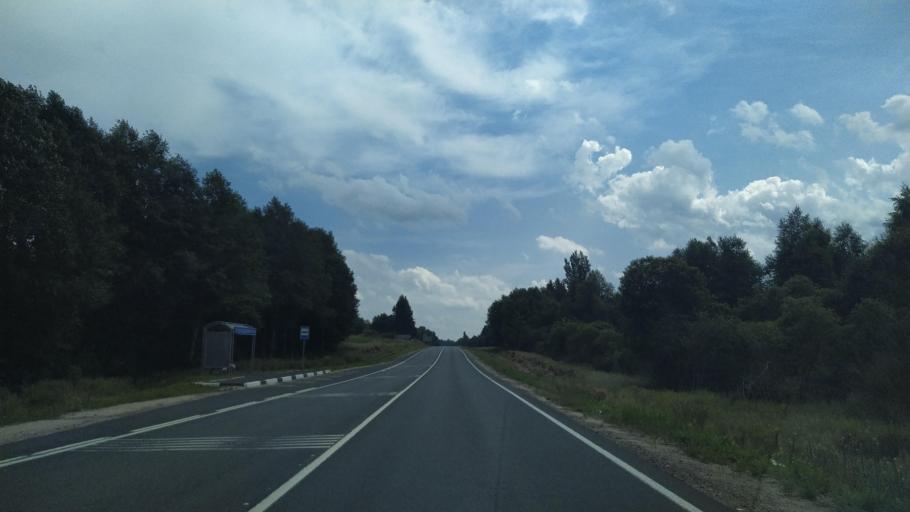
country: RU
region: Pskov
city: Pskov
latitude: 57.8140
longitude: 28.6944
